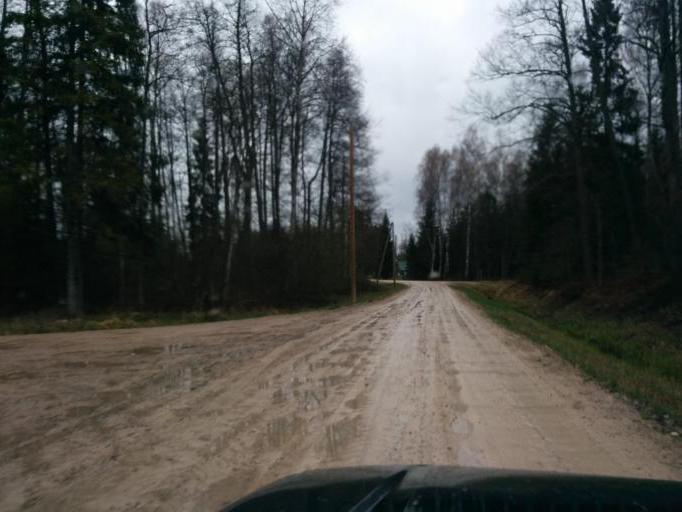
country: LV
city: Tireli
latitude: 56.8275
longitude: 23.7016
